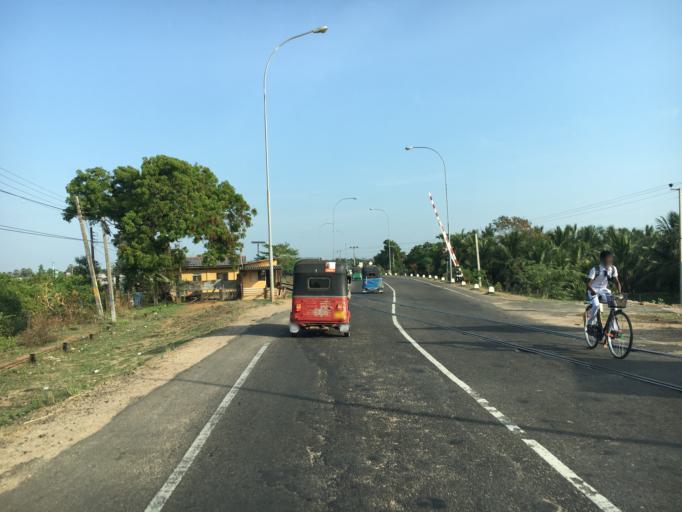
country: LK
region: Eastern Province
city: Eravur Town
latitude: 7.9196
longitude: 81.5170
